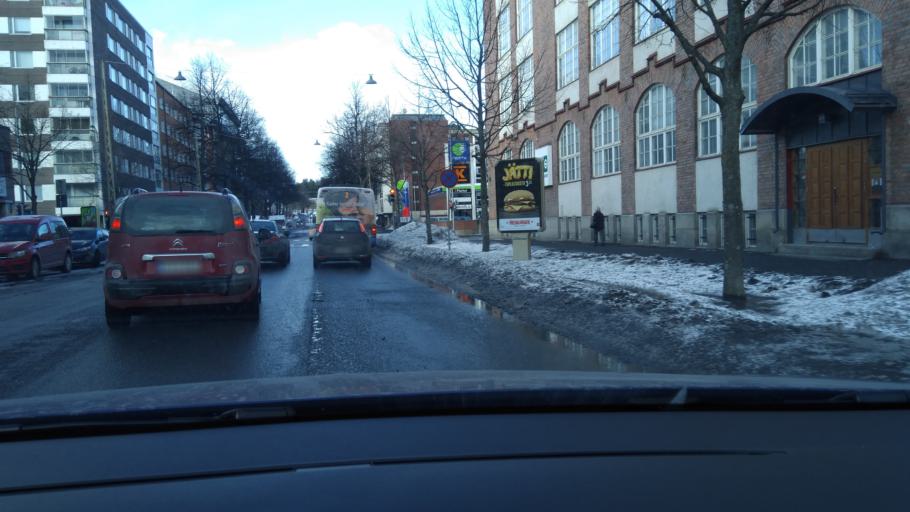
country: FI
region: Pirkanmaa
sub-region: Tampere
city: Tampere
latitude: 61.5026
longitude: 23.7796
